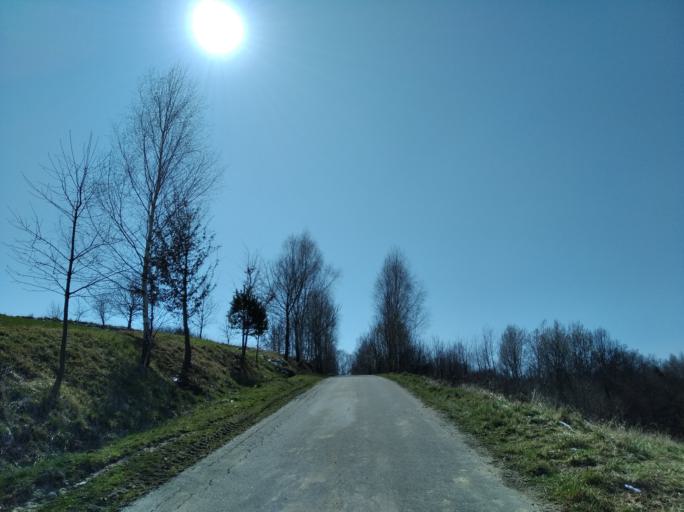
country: PL
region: Subcarpathian Voivodeship
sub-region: Powiat strzyzowski
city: Strzyzow
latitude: 49.8593
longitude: 21.8119
